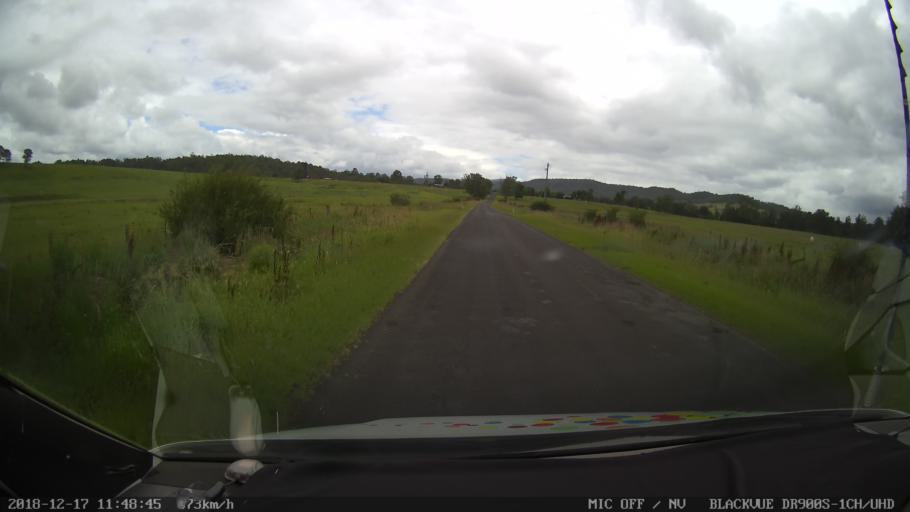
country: AU
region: New South Wales
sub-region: Kyogle
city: Kyogle
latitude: -28.6137
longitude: 152.5922
